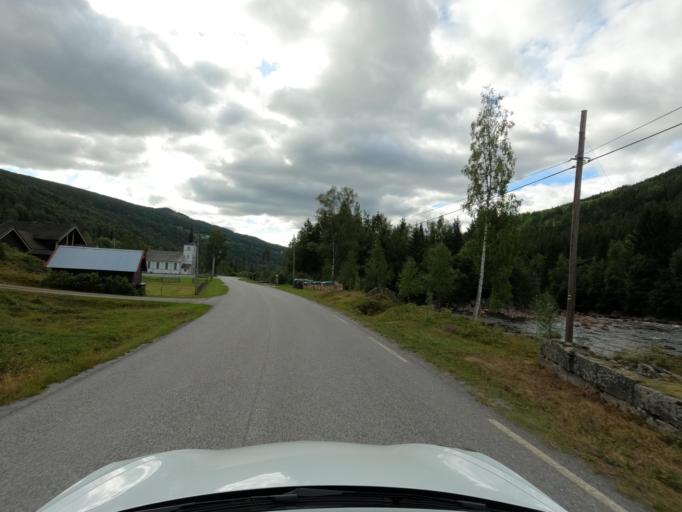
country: NO
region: Buskerud
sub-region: Nore og Uvdal
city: Rodberg
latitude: 60.0307
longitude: 8.8242
